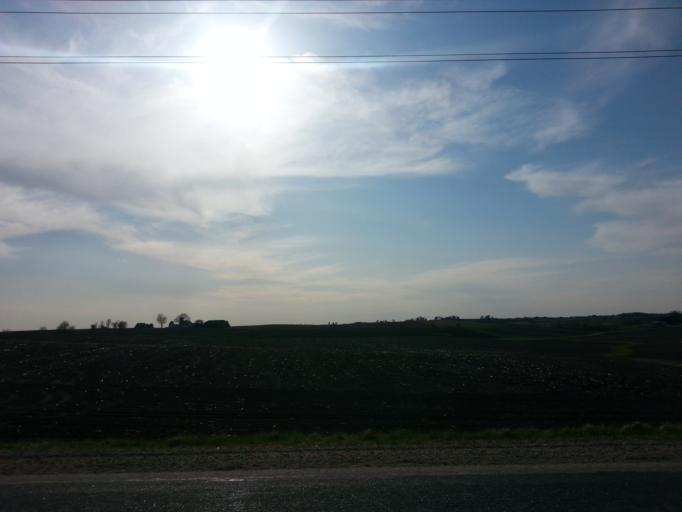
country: US
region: Wisconsin
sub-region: Pierce County
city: Ellsworth
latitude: 44.7123
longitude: -92.6091
